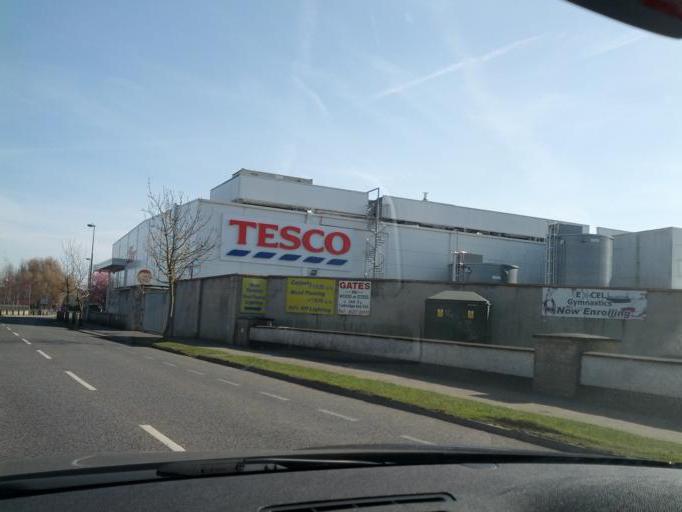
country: IE
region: Leinster
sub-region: Kildare
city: Celbridge
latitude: 53.3442
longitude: -6.5463
